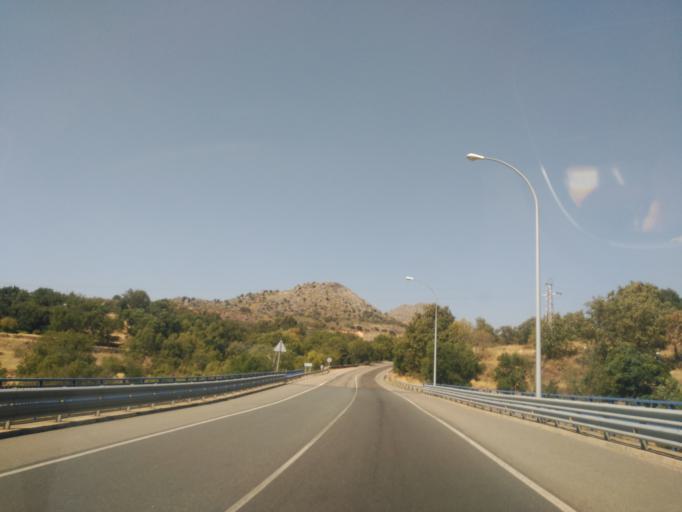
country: ES
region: Castille and Leon
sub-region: Provincia de Salamanca
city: Bejar
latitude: 40.3924
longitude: -5.7405
